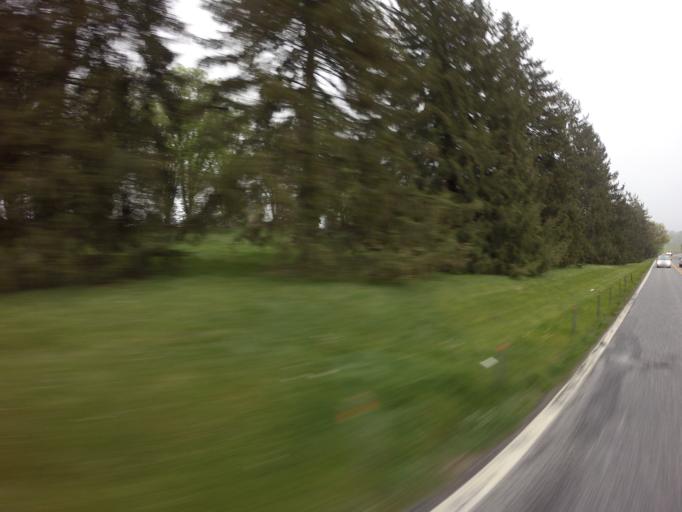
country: US
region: Maryland
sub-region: Baltimore County
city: Reisterstown
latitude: 39.4817
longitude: -76.7855
